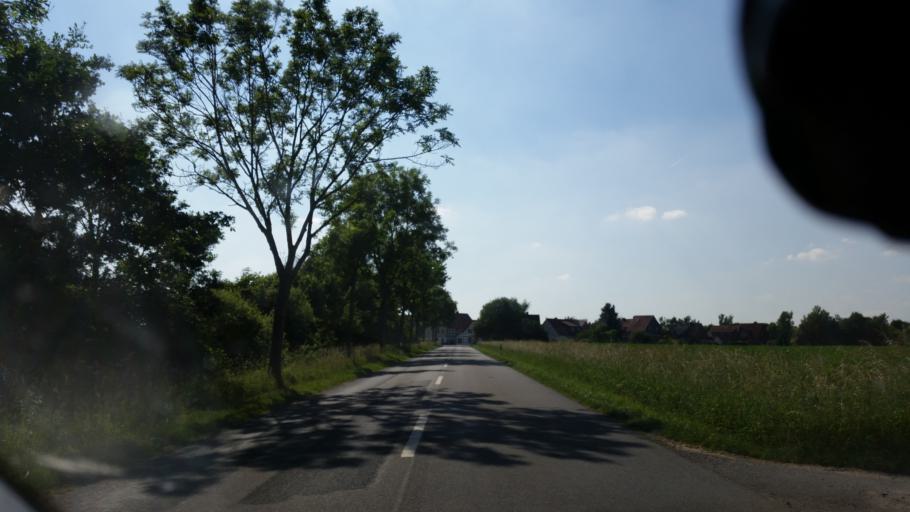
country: DE
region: Lower Saxony
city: Konigslutter am Elm
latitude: 52.3118
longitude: 10.7824
